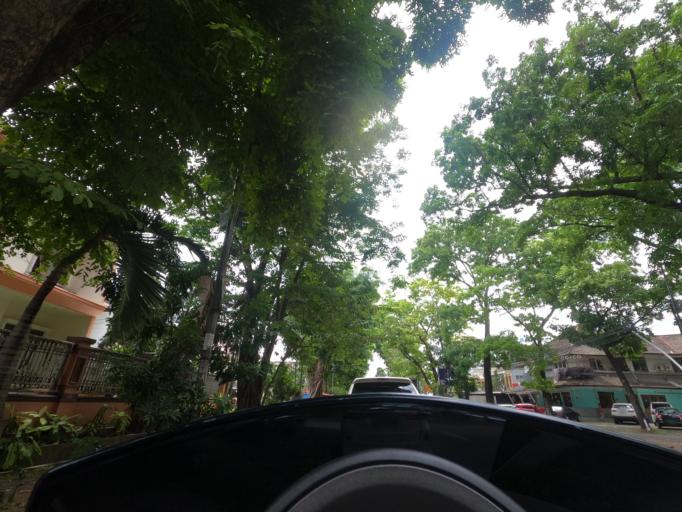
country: ID
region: West Java
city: Bandung
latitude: -6.8978
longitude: 107.6143
